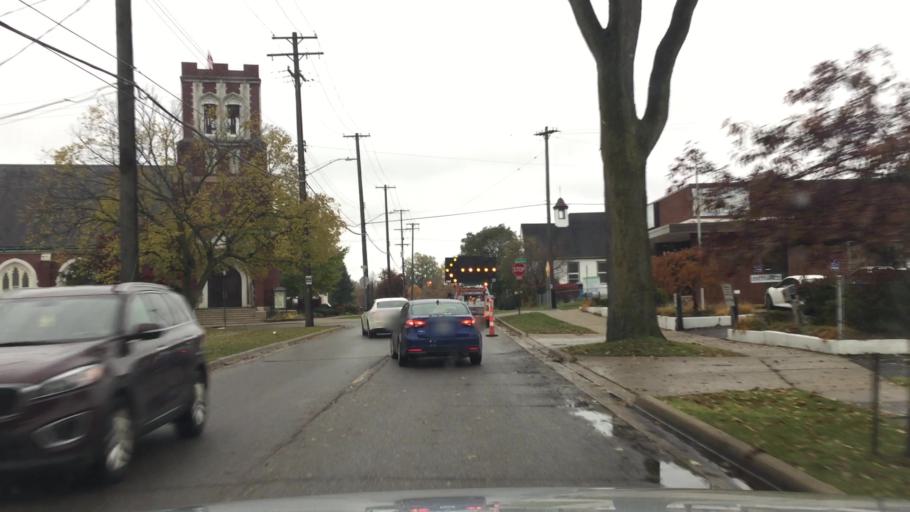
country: US
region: Michigan
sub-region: Oakland County
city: Pontiac
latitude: 42.6359
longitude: -83.2989
